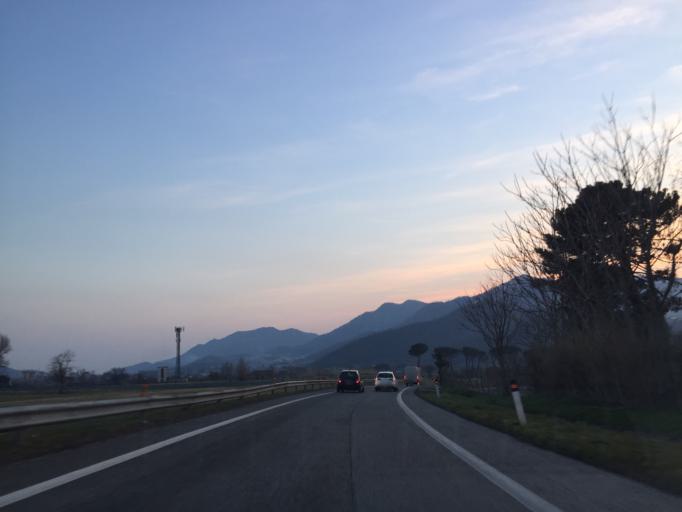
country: IT
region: Campania
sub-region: Provincia di Salerno
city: Fisciano
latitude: 40.7740
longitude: 14.7837
